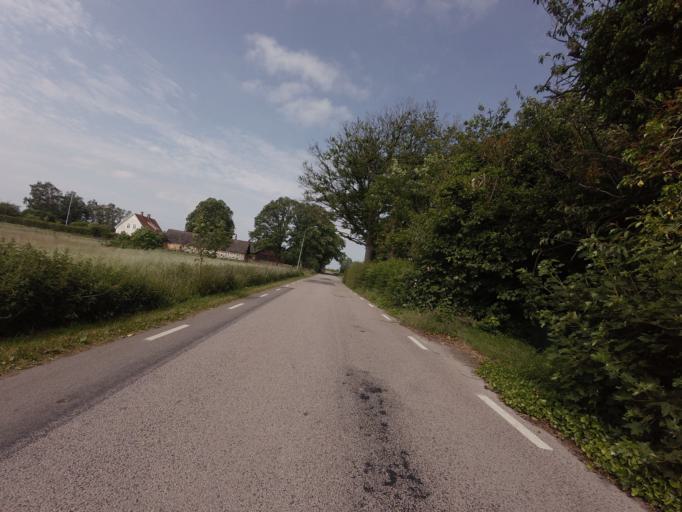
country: SE
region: Skane
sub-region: Hoganas Kommun
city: Hoganas
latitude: 56.1879
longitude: 12.6395
